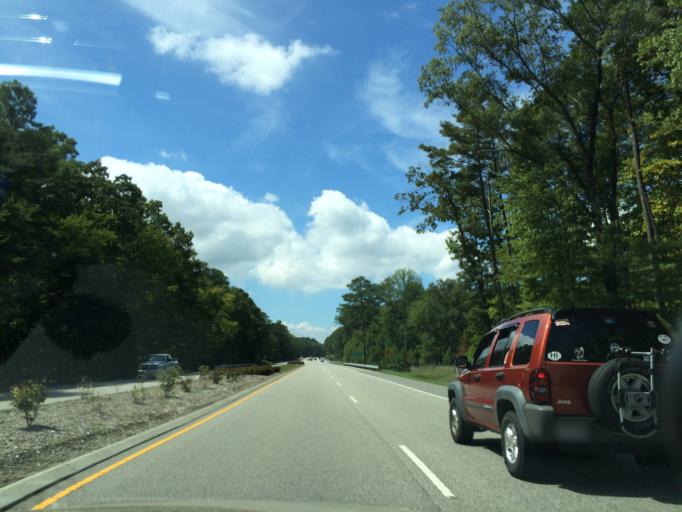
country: US
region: Virginia
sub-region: York County
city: Yorktown
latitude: 37.1800
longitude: -76.5143
